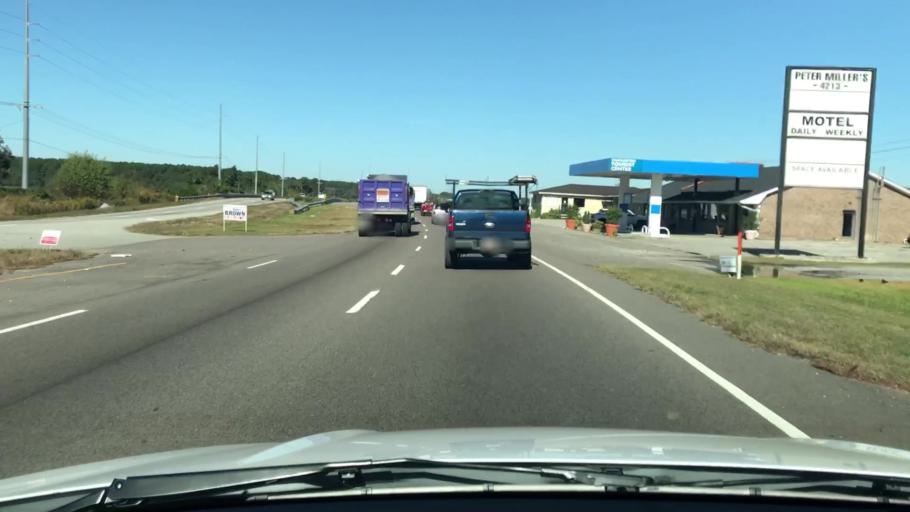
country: US
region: South Carolina
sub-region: Charleston County
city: Shell Point
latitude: 32.7860
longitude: -80.1467
